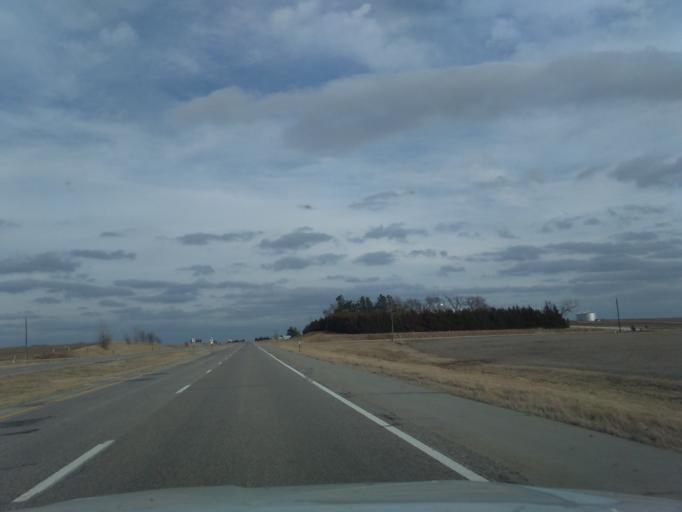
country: US
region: Nebraska
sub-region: Lancaster County
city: Hickman
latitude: 40.4654
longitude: -96.7251
